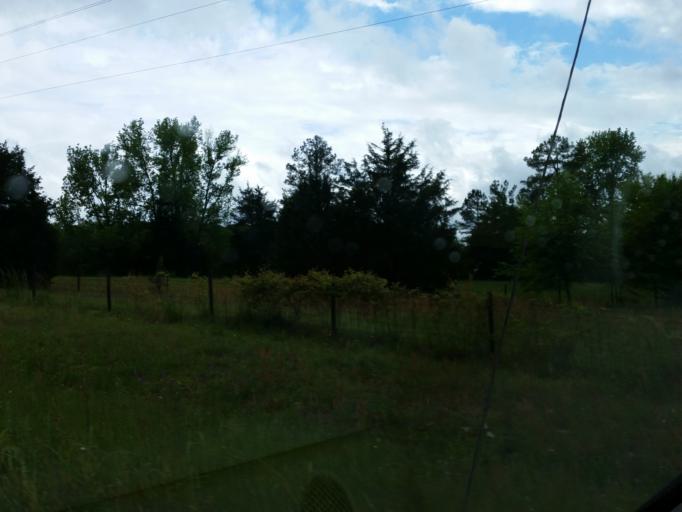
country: US
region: Georgia
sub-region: Lamar County
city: Barnesville
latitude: 33.0072
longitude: -84.1226
